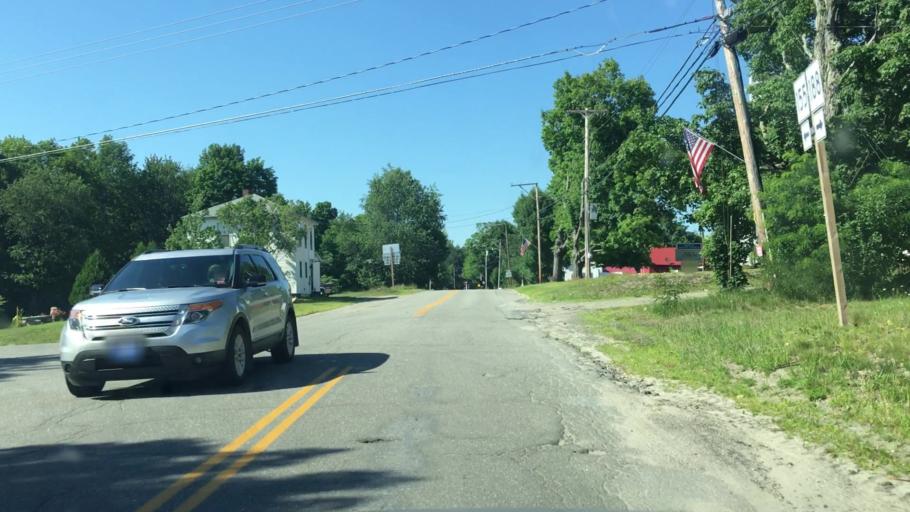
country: US
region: Maine
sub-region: Penobscot County
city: Enfield
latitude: 45.2486
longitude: -68.5658
